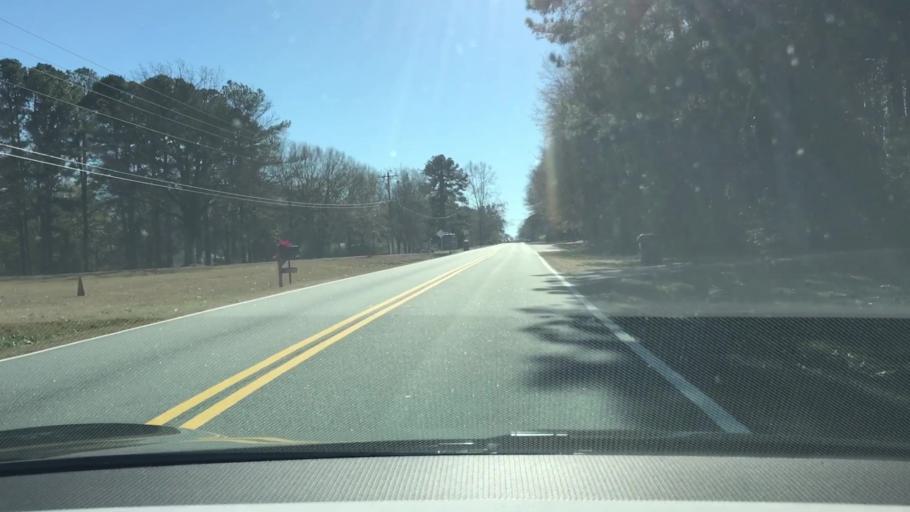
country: US
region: Georgia
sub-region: Walton County
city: Monroe
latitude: 33.8554
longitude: -83.7368
